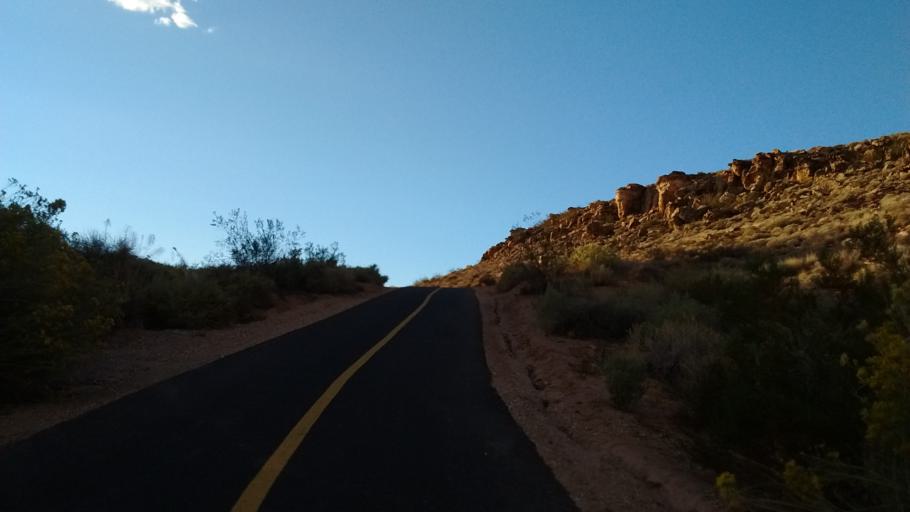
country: US
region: Utah
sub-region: Washington County
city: Washington
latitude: 37.1286
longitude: -113.4838
